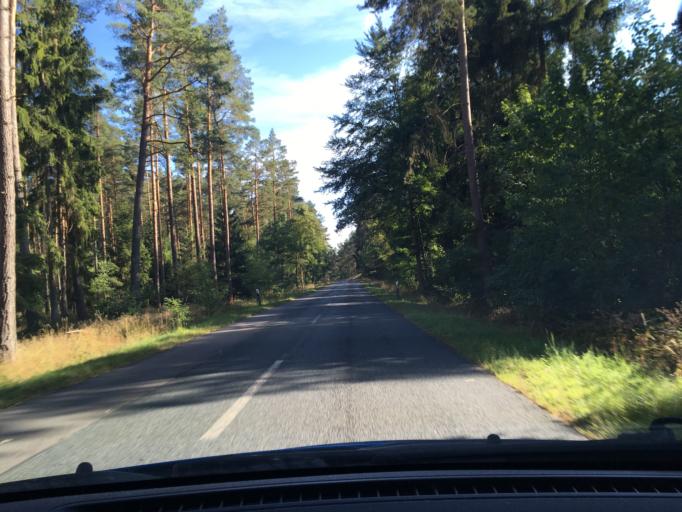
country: DE
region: Lower Saxony
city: Thomasburg
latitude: 53.2389
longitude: 10.7047
